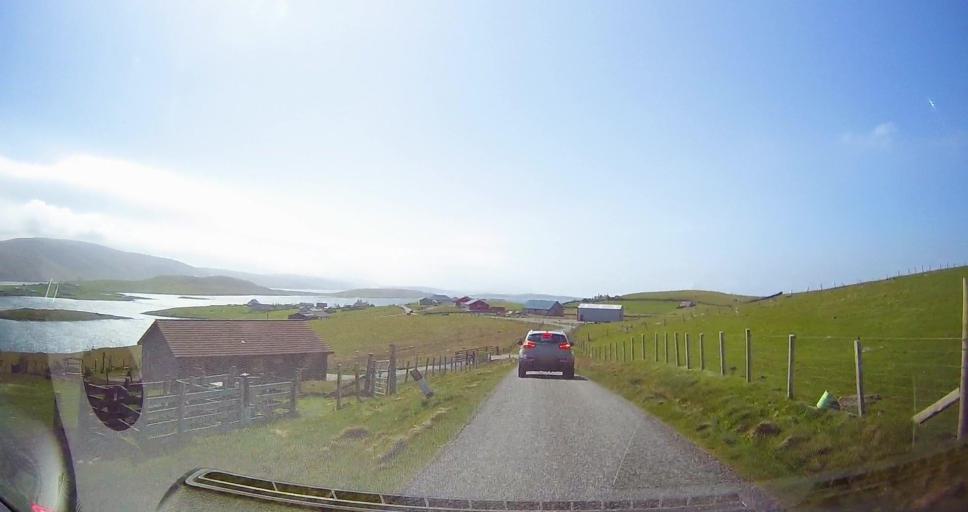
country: GB
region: Scotland
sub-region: Shetland Islands
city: Sandwick
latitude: 60.0730
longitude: -1.3398
